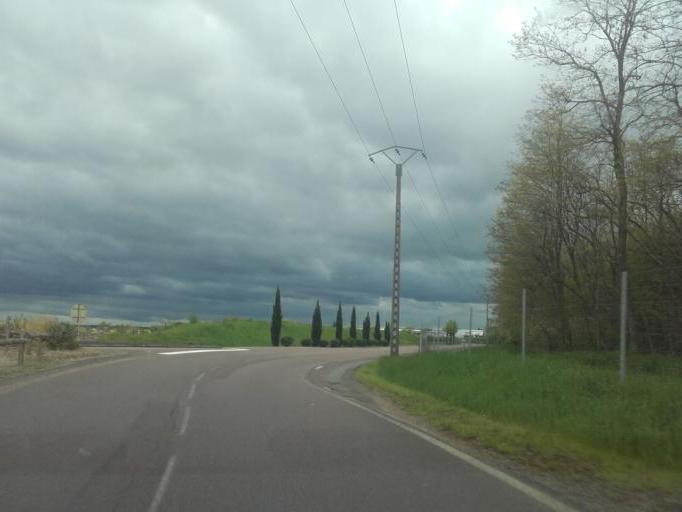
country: FR
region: Bourgogne
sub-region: Departement de la Cote-d'Or
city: Beaune
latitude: 47.0268
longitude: 4.8756
